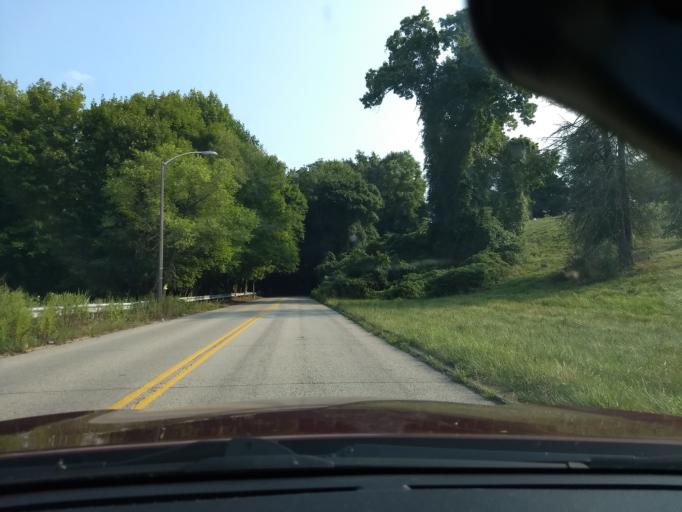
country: US
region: Pennsylvania
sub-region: Allegheny County
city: Aspinwall
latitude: 40.4758
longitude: -79.8983
